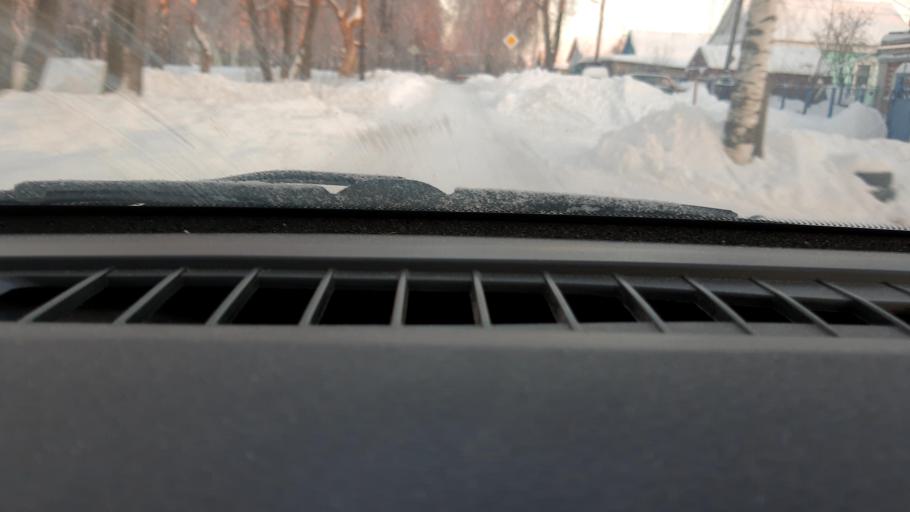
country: RU
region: Nizjnij Novgorod
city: Kstovo
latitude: 56.1736
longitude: 44.1736
